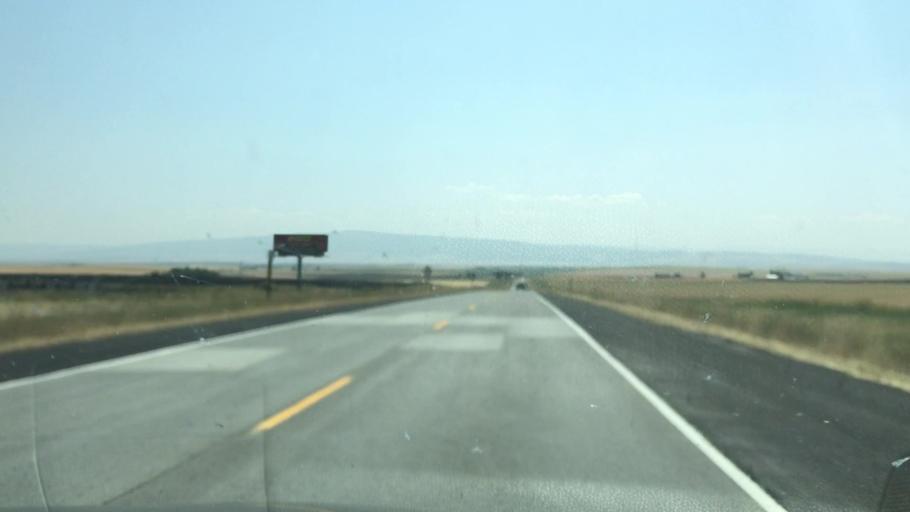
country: US
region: Idaho
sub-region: Lewis County
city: Nezperce
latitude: 46.0352
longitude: -116.3359
